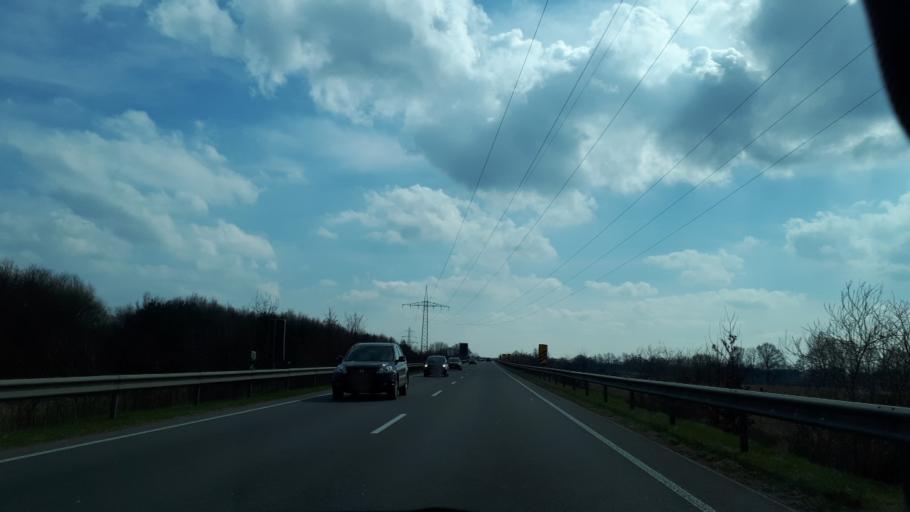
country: DE
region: Lower Saxony
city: Vechta
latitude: 52.7235
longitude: 8.2549
